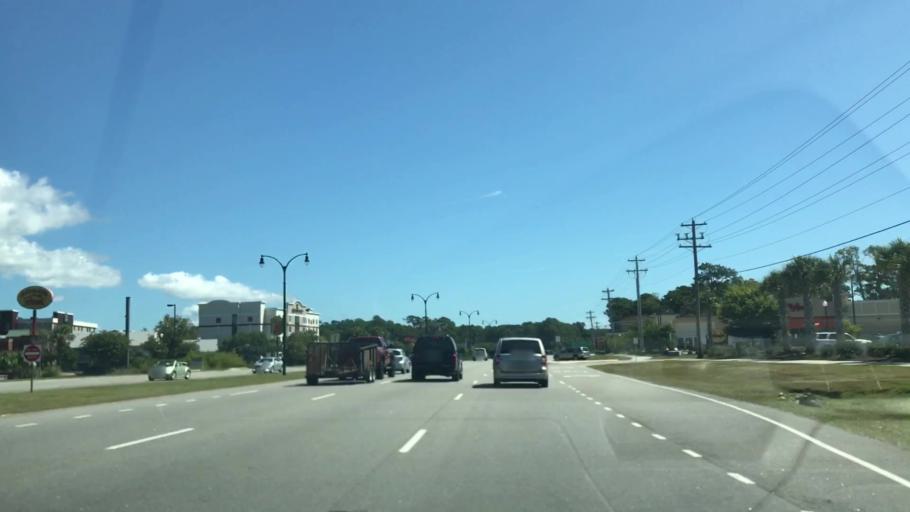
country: US
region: South Carolina
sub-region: Horry County
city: North Myrtle Beach
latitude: 33.8430
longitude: -78.6602
